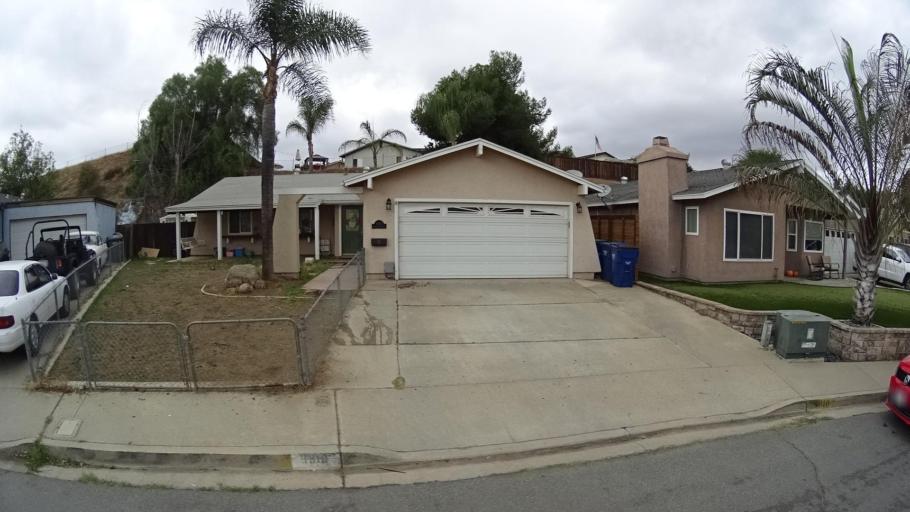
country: US
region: California
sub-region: San Diego County
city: Lakeside
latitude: 32.8608
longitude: -116.9043
